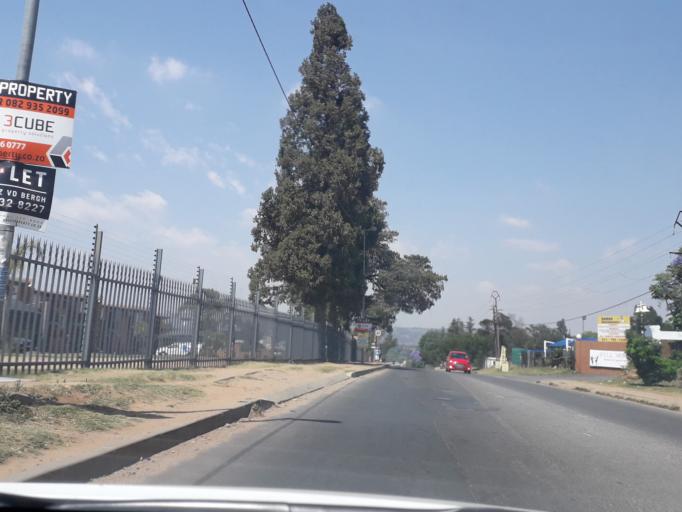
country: ZA
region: Gauteng
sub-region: West Rand District Municipality
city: Muldersdriseloop
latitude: -26.0729
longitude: 27.9132
